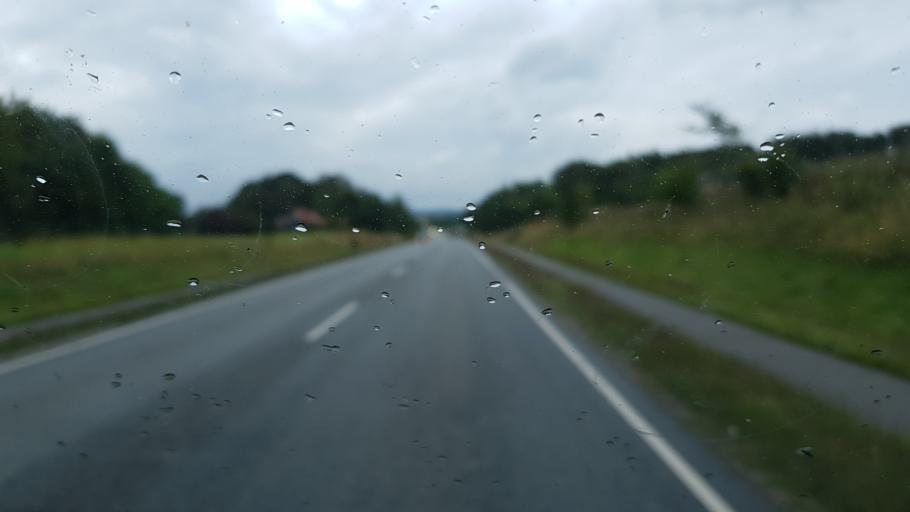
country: DK
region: Central Jutland
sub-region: Horsens Kommune
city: Horsens
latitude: 55.9011
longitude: 9.7471
